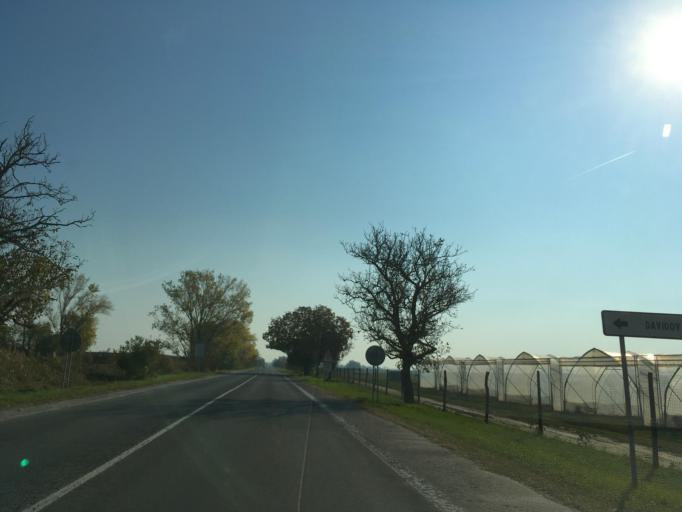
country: SK
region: Trnavsky
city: Samorin
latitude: 48.0566
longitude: 17.2853
